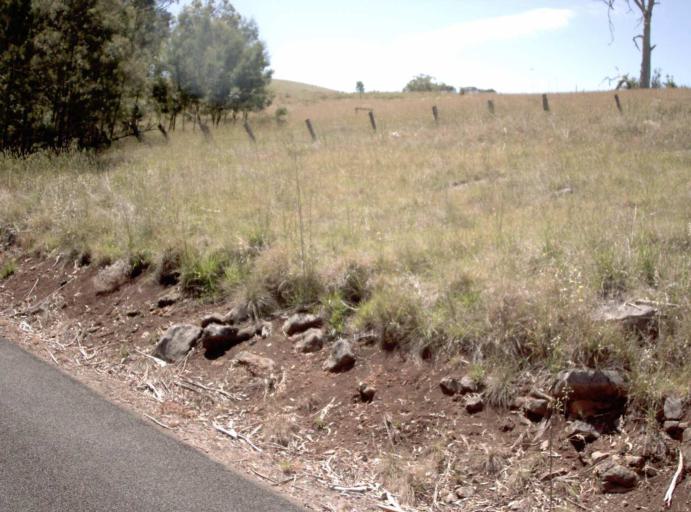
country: AU
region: Victoria
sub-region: East Gippsland
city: Lakes Entrance
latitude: -37.4364
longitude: 148.1942
